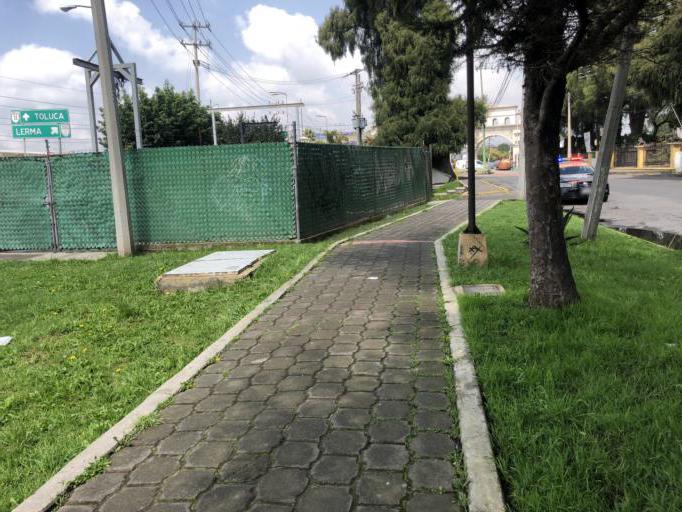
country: MX
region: Mexico
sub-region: Ocoyoacac
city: San Antonio el Llanito
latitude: 19.2845
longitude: -99.4999
